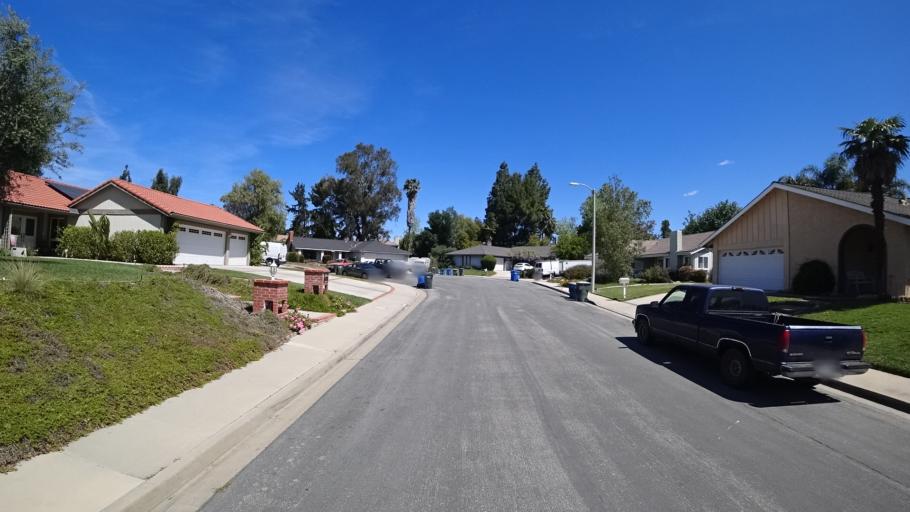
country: US
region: California
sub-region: Ventura County
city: Thousand Oaks
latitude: 34.2197
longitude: -118.8749
